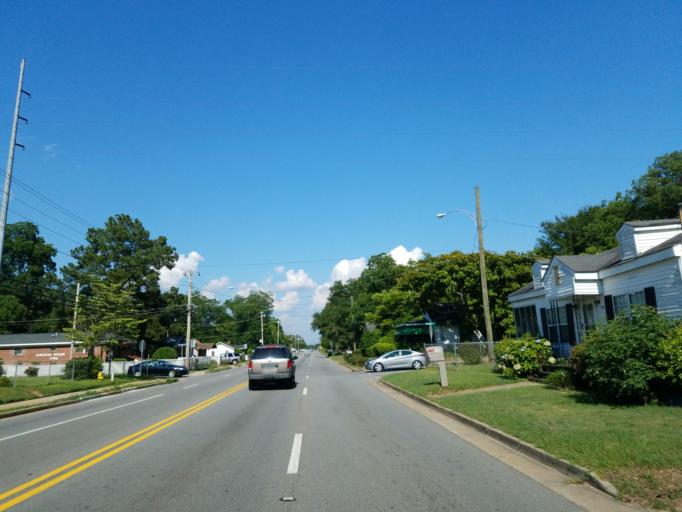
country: US
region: Georgia
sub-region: Peach County
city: Fort Valley
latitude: 32.5539
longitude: -83.8792
